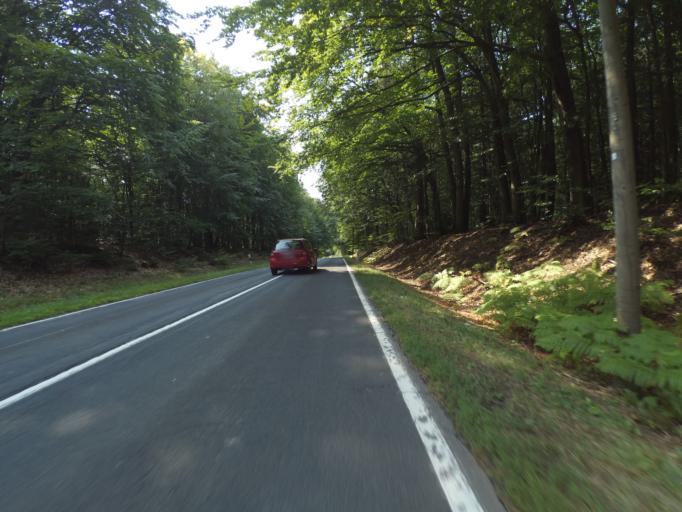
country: DE
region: Saarland
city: Britten
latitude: 49.5189
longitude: 6.6599
